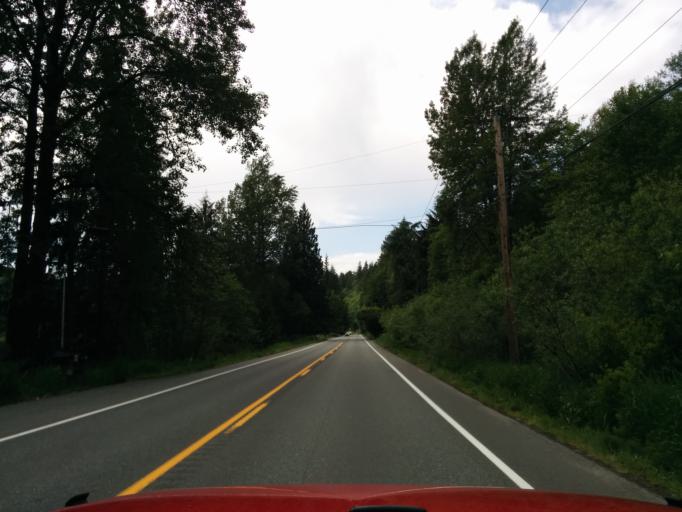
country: US
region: Washington
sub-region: King County
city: Ames Lake
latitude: 47.6270
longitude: -121.9809
